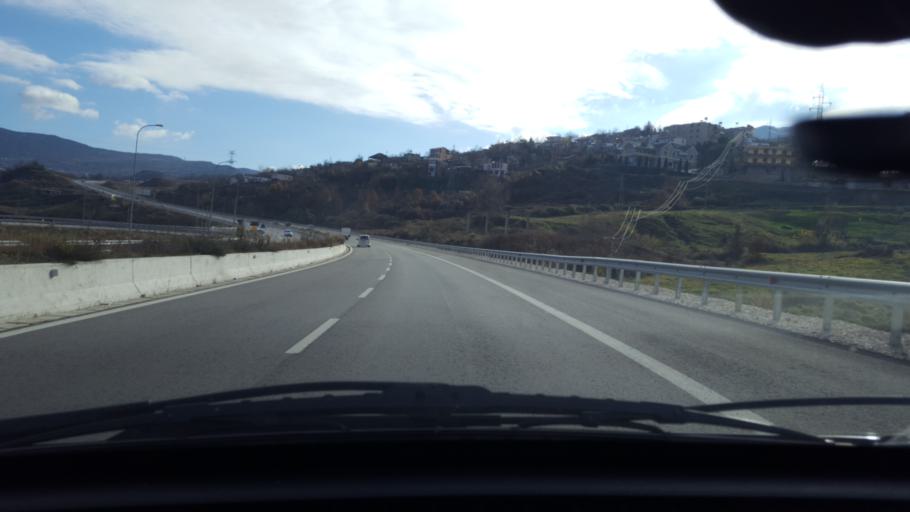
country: AL
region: Tirane
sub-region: Rrethi i Tiranes
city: Berzhite
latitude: 41.2288
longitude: 19.9304
